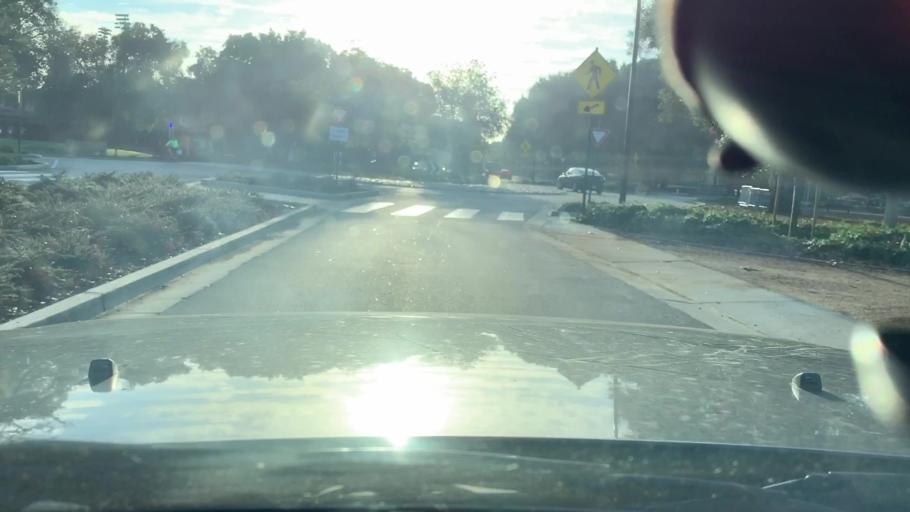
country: US
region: California
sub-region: Santa Clara County
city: Stanford
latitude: 37.4317
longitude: -122.1645
